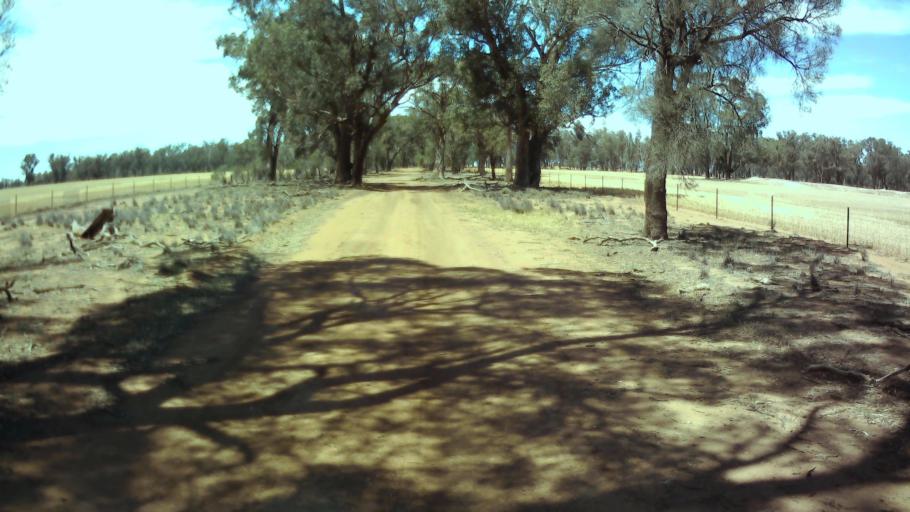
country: AU
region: New South Wales
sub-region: Weddin
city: Grenfell
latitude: -33.9072
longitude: 147.8072
